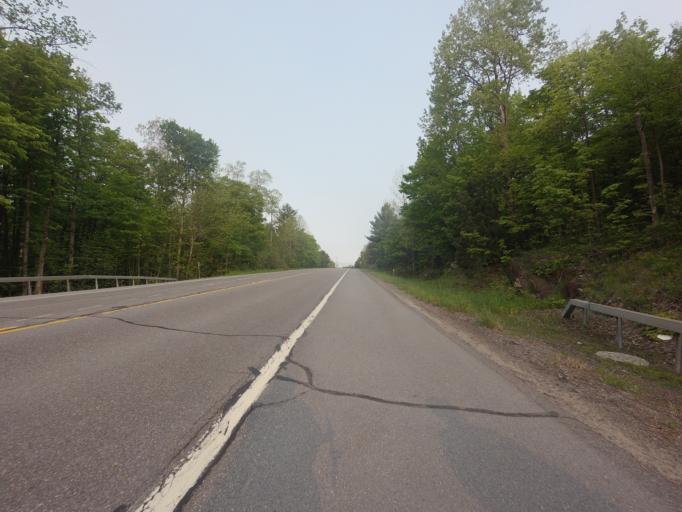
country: US
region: New York
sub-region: Jefferson County
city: Carthage
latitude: 44.0742
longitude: -75.4642
